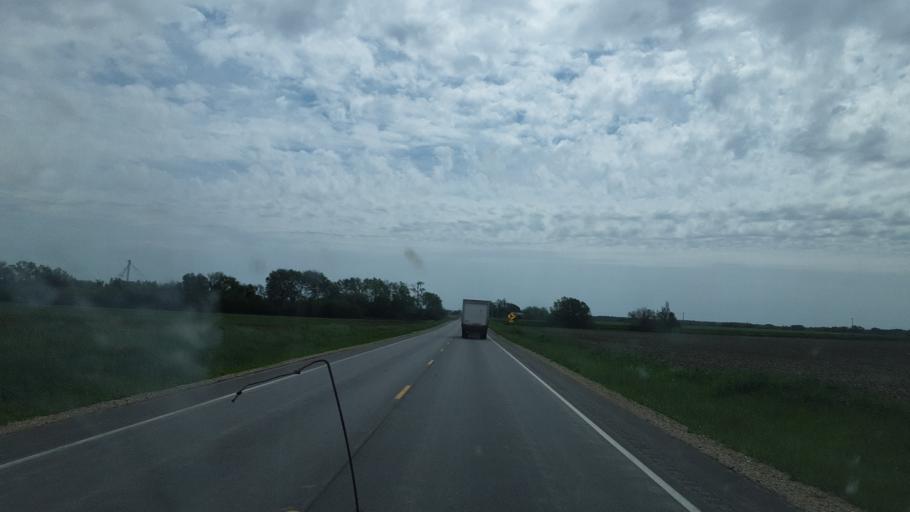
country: US
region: Illinois
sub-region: Tazewell County
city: Richmond
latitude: 40.3096
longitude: -89.3720
